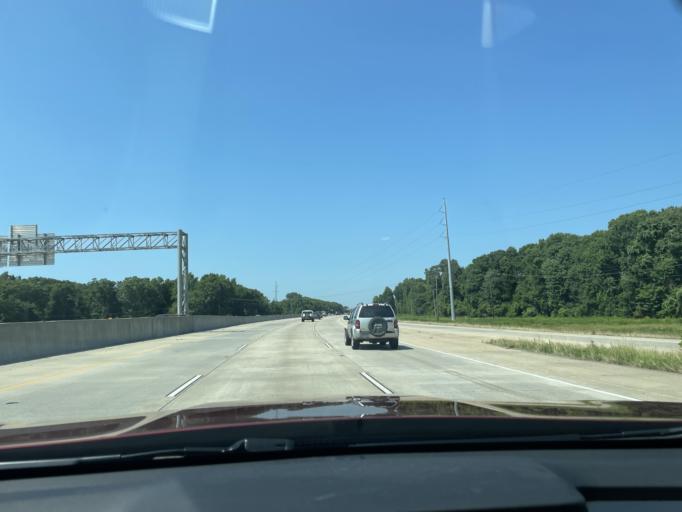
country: US
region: Arkansas
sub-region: Pulaski County
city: Jacksonville
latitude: 34.8581
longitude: -92.1324
